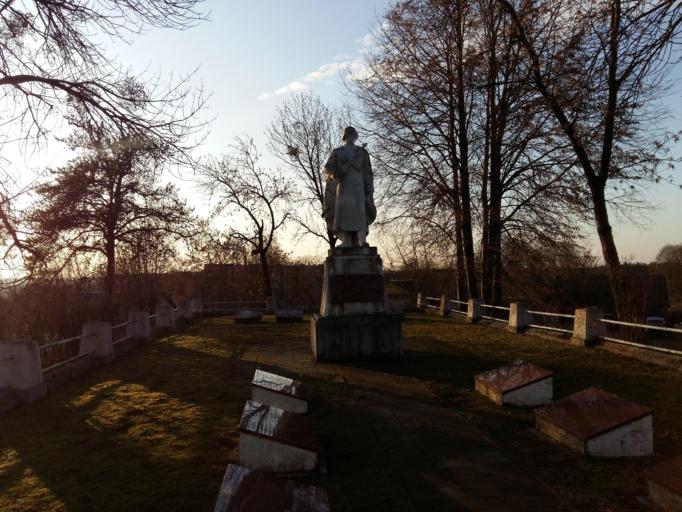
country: LT
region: Alytaus apskritis
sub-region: Alytaus rajonas
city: Daugai
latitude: 54.1645
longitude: 24.1851
